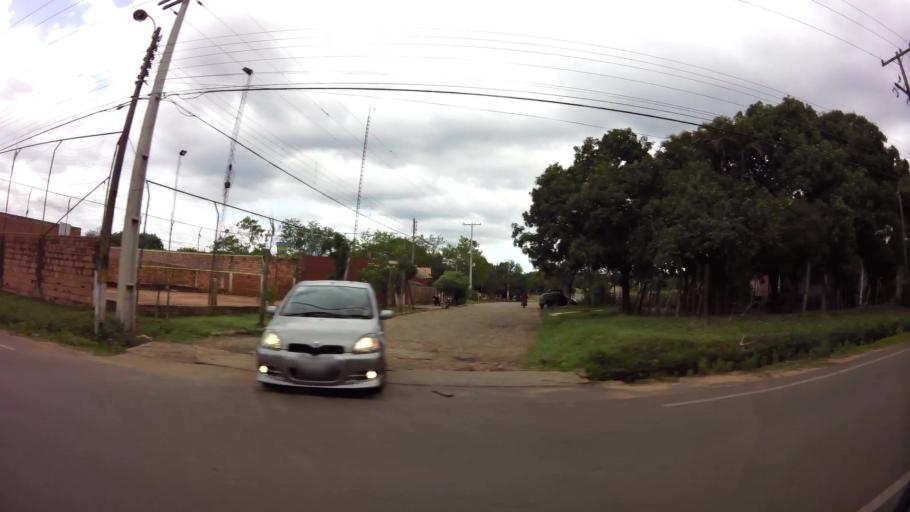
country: PY
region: Central
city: San Lorenzo
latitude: -25.2887
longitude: -57.4877
